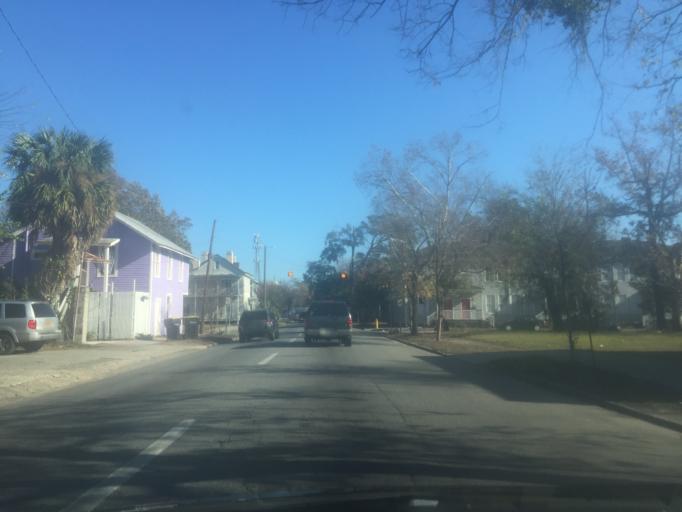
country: US
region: Georgia
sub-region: Chatham County
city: Savannah
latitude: 32.0635
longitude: -81.1021
